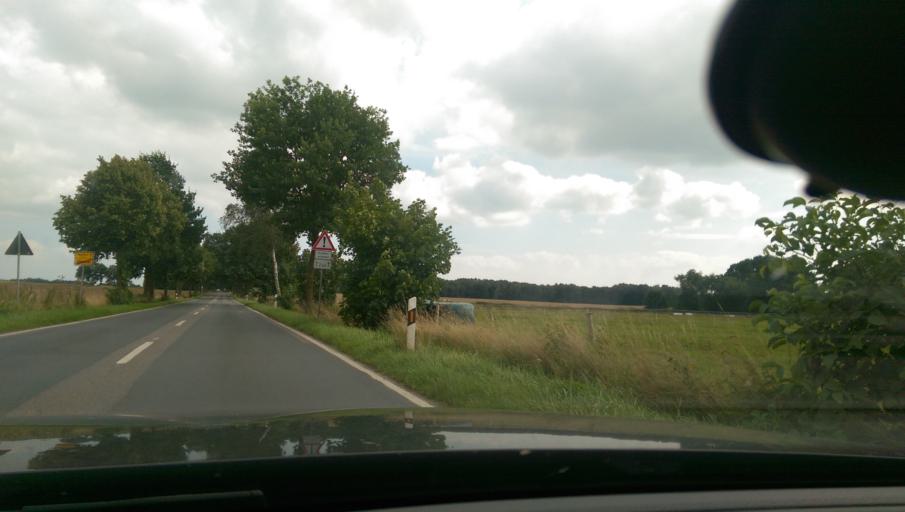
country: DE
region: Lower Saxony
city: Lindwedel
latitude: 52.5669
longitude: 9.6205
